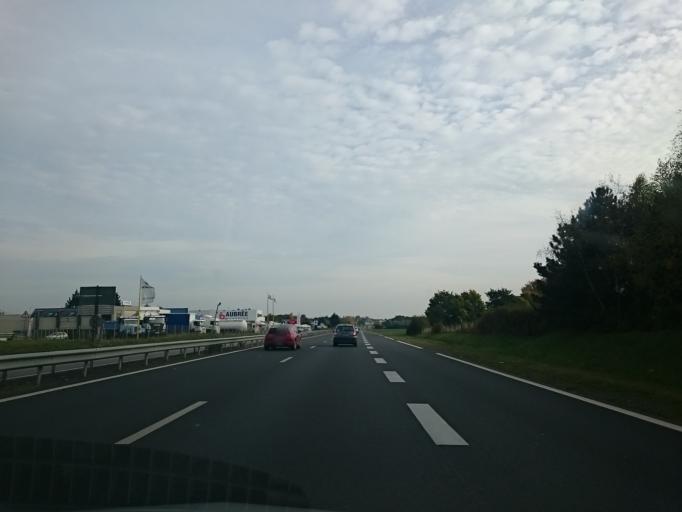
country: FR
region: Brittany
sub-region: Departement d'Ille-et-Vilaine
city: Vern-sur-Seiche
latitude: 48.0610
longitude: -1.6159
